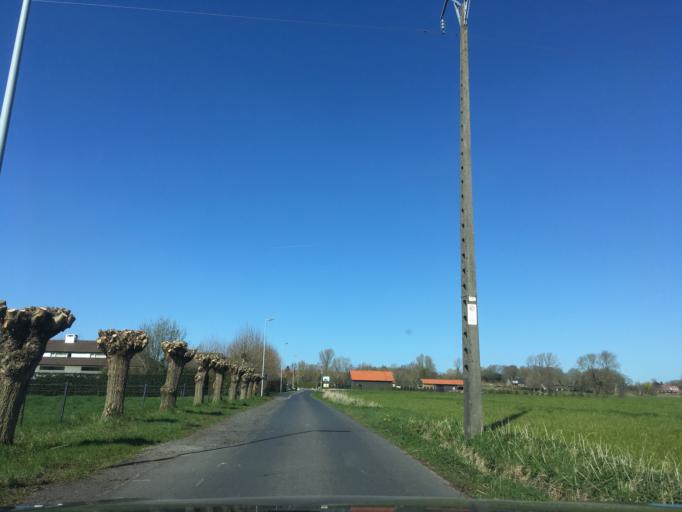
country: BE
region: Flanders
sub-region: Provincie West-Vlaanderen
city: Hooglede
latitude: 50.9721
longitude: 3.0920
